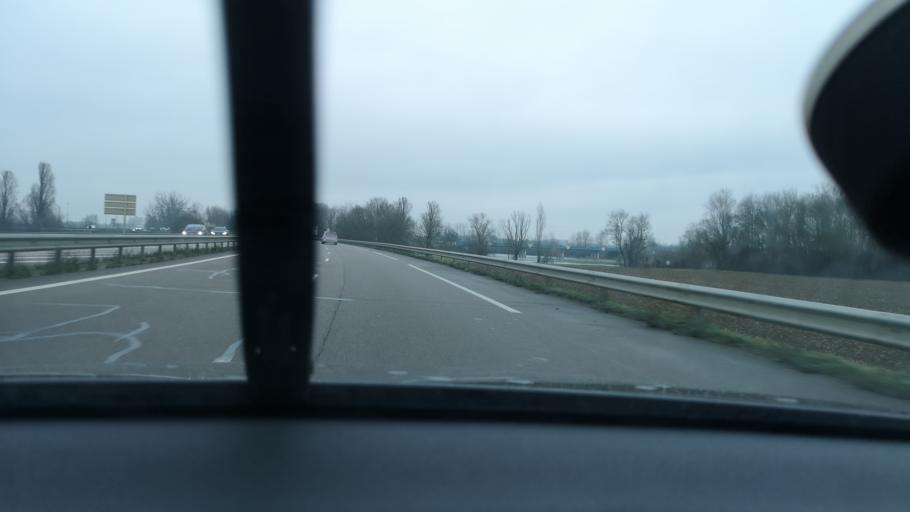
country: FR
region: Bourgogne
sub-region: Departement de Saone-et-Loire
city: Saint-Marcel
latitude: 46.7747
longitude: 4.8757
